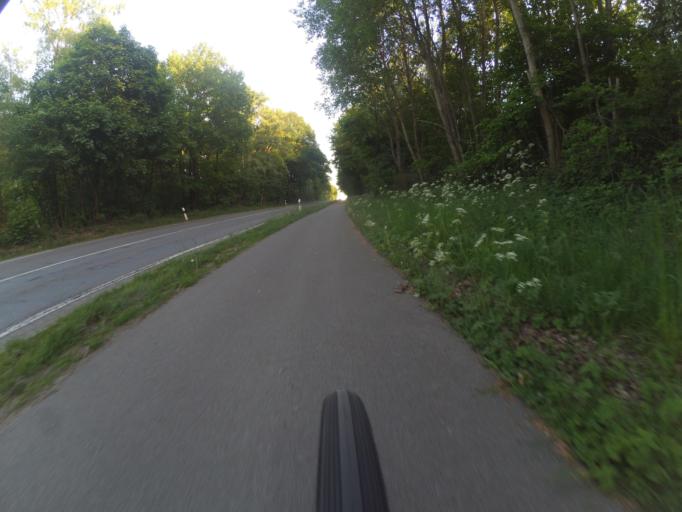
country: DE
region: North Rhine-Westphalia
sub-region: Regierungsbezirk Munster
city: Hopsten
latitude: 52.3350
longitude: 7.6630
